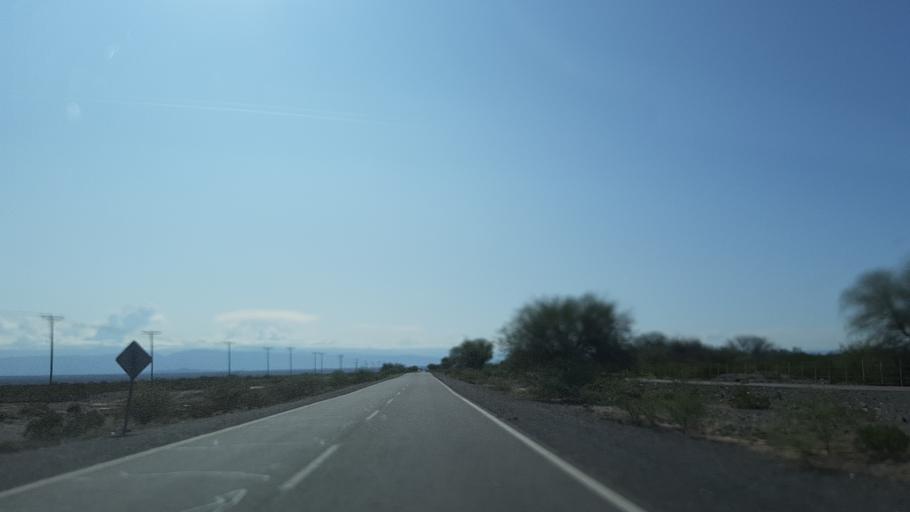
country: AR
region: San Juan
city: Caucete
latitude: -31.7570
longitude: -68.0739
